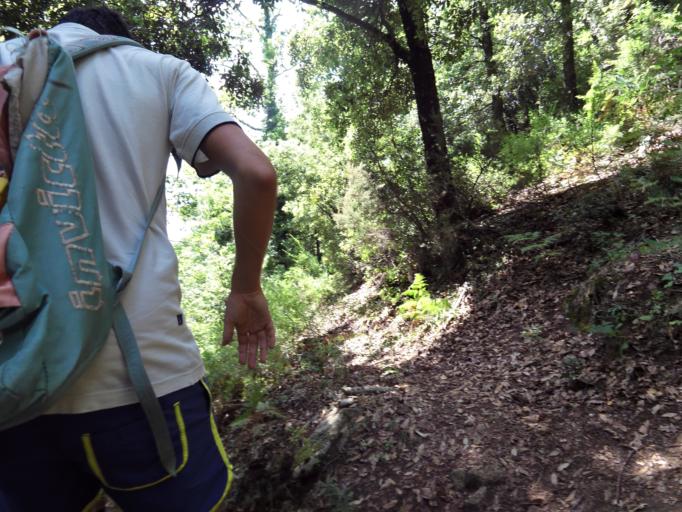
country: IT
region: Calabria
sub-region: Provincia di Vibo-Valentia
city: Nardodipace
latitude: 38.5080
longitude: 16.3863
